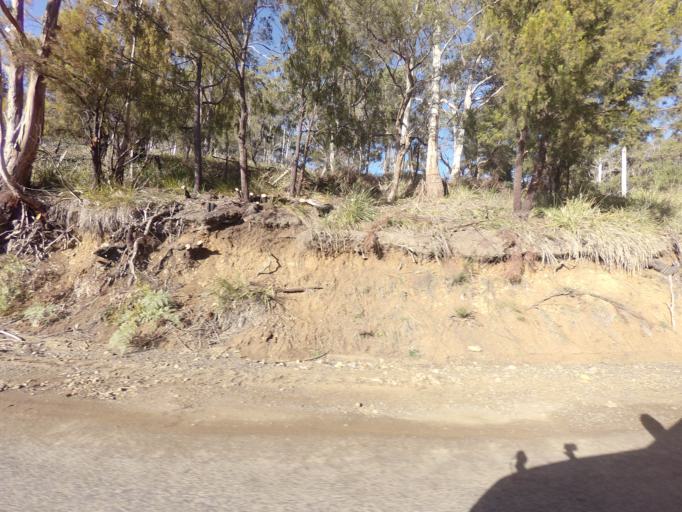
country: AU
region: Tasmania
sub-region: Glenorchy
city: Berriedale
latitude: -42.8134
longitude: 147.1744
